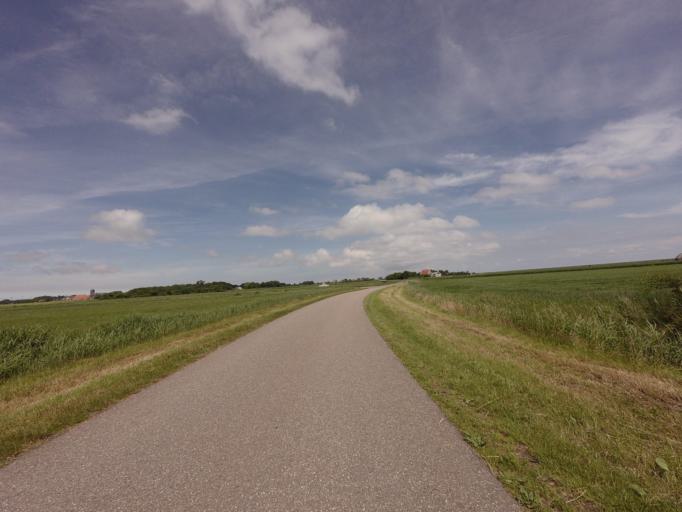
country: NL
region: North Holland
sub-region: Gemeente Texel
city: Den Burg
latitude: 53.0775
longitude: 4.8807
